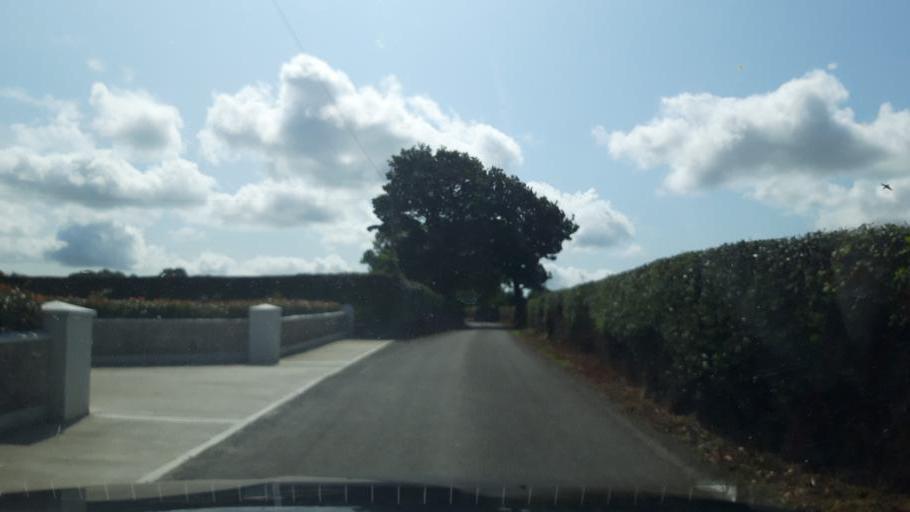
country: IE
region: Leinster
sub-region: Kilkenny
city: Graiguenamanagh
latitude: 52.5761
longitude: -6.9859
